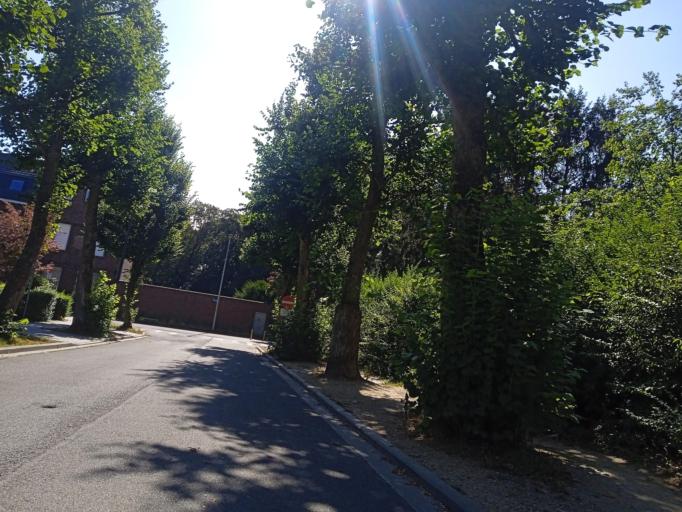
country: BE
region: Flanders
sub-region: Provincie Vlaams-Brabant
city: Drogenbos
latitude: 50.8136
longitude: 4.2843
